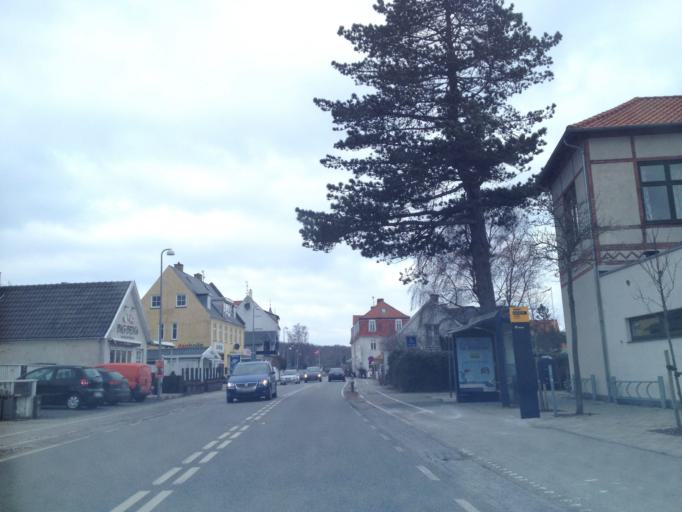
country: DK
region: Capital Region
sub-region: Helsingor Kommune
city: Espergaerde
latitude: 55.9916
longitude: 12.5603
